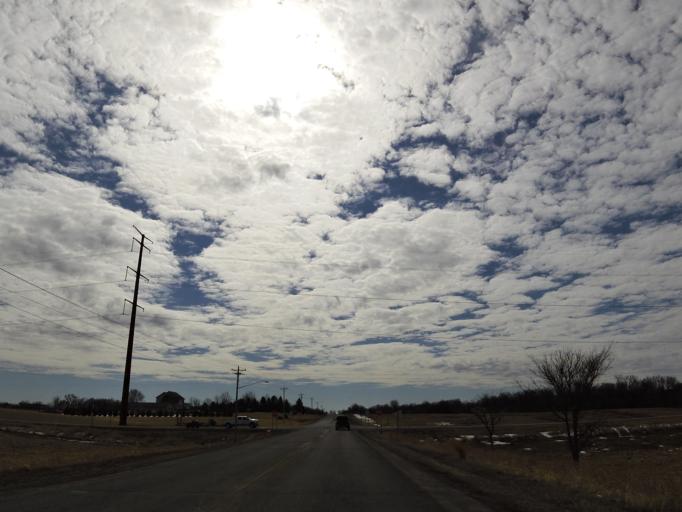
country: US
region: Minnesota
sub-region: Le Sueur County
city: New Prague
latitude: 44.5739
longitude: -93.5569
